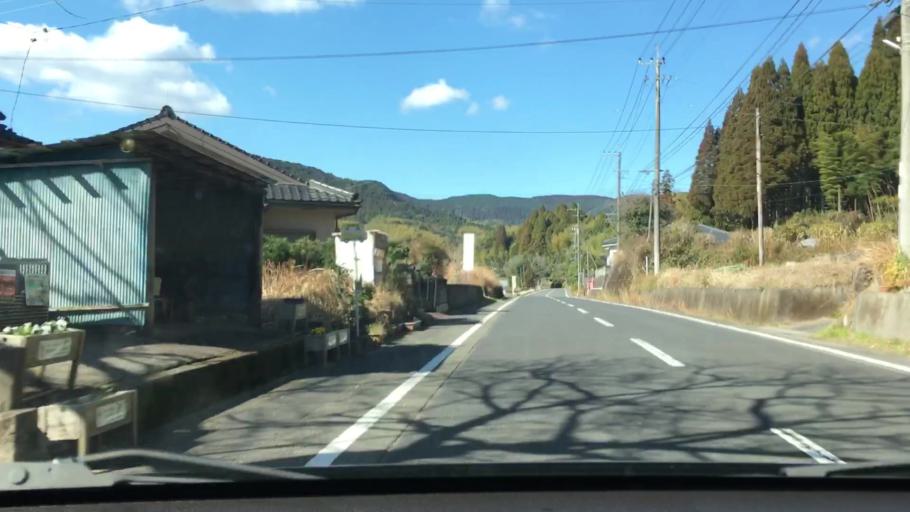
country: JP
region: Kagoshima
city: Ijuin
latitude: 31.7047
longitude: 130.4466
